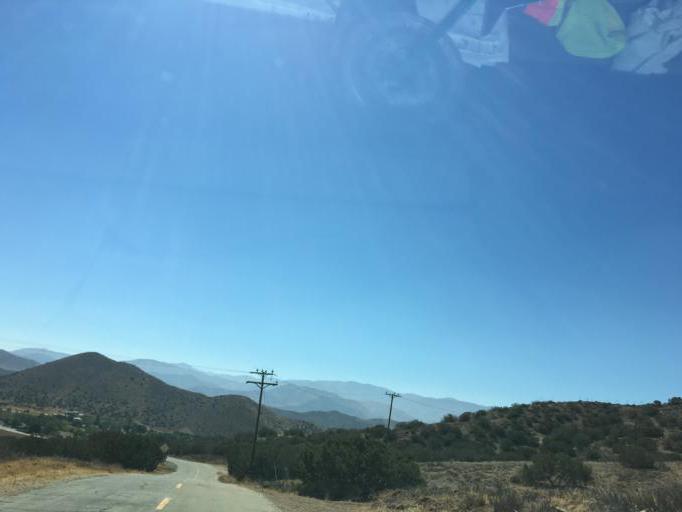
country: US
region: California
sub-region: Los Angeles County
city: Acton
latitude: 34.5075
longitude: -118.2036
